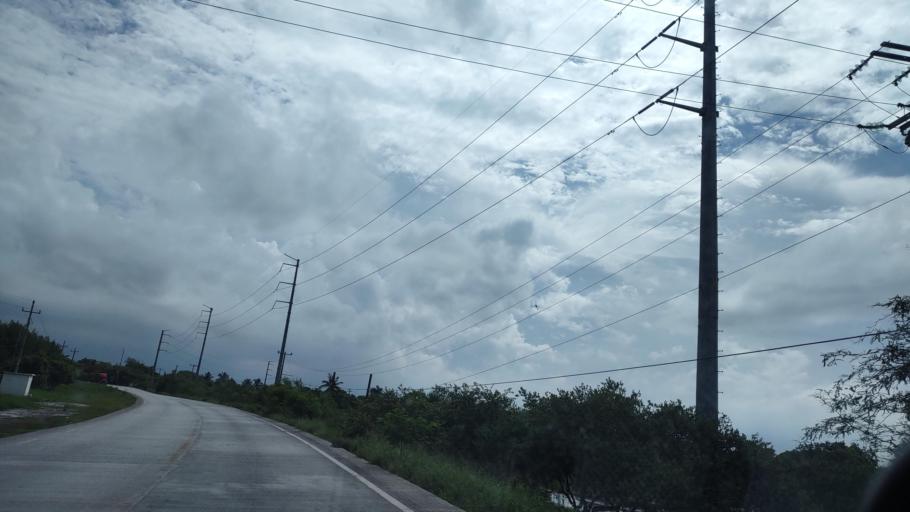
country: MX
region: Veracruz
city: Anahuac
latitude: 22.2069
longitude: -97.8688
